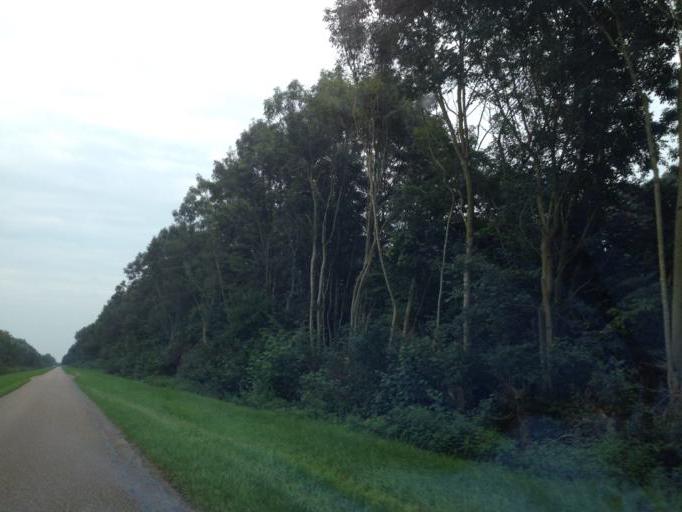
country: NL
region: Flevoland
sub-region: Gemeente Lelystad
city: Lelystad
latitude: 52.4220
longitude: 5.4132
